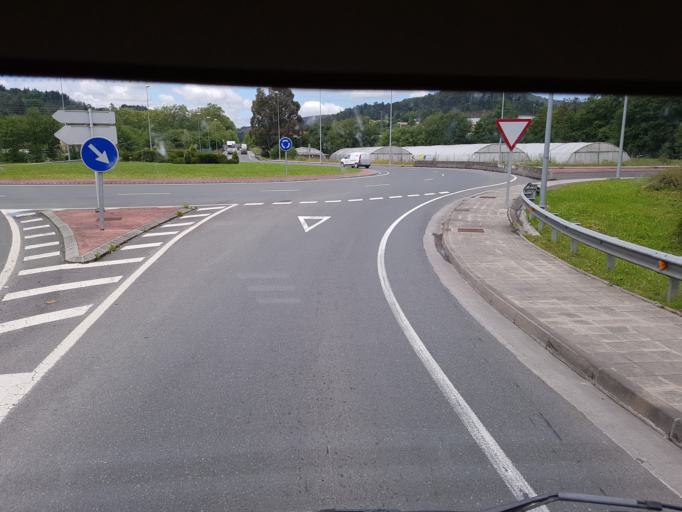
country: ES
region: Basque Country
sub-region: Bizkaia
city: Amorebieta
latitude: 43.2293
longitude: -2.7566
